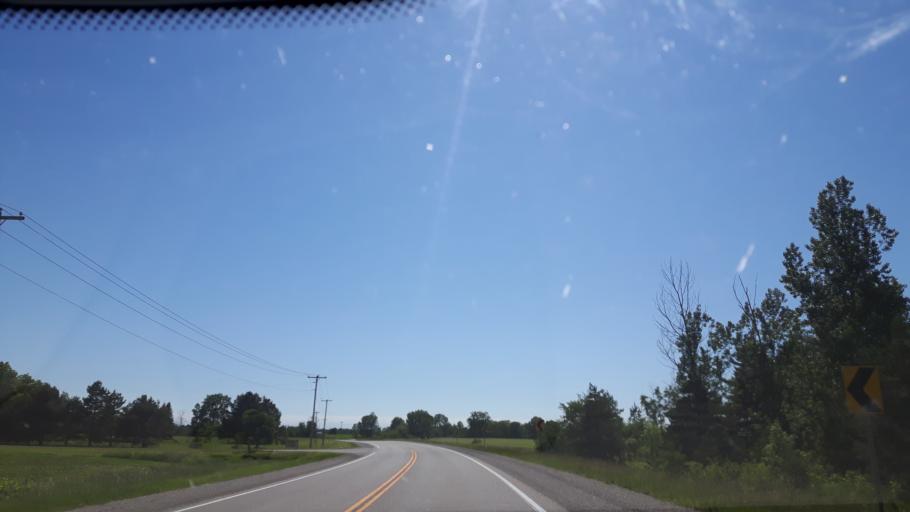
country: CA
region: Ontario
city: Bluewater
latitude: 43.4147
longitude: -81.6860
